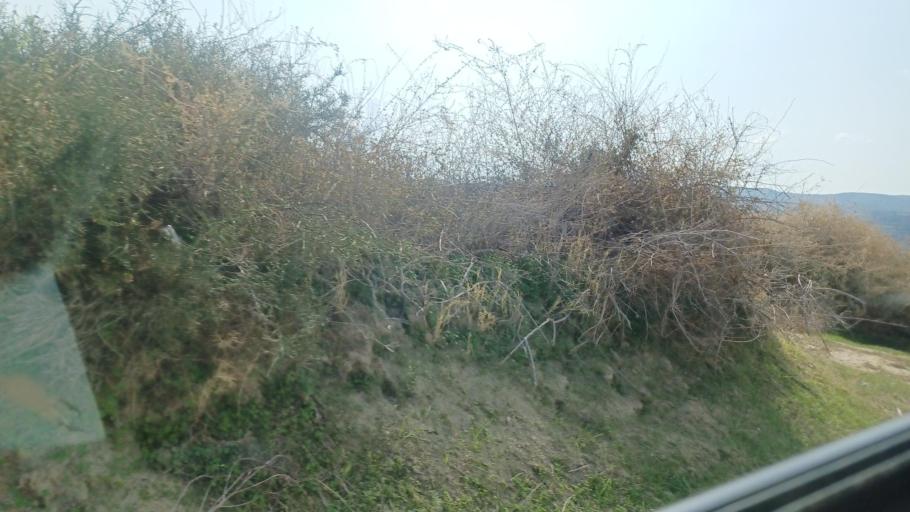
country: CY
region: Pafos
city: Polis
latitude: 35.0003
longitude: 32.4613
